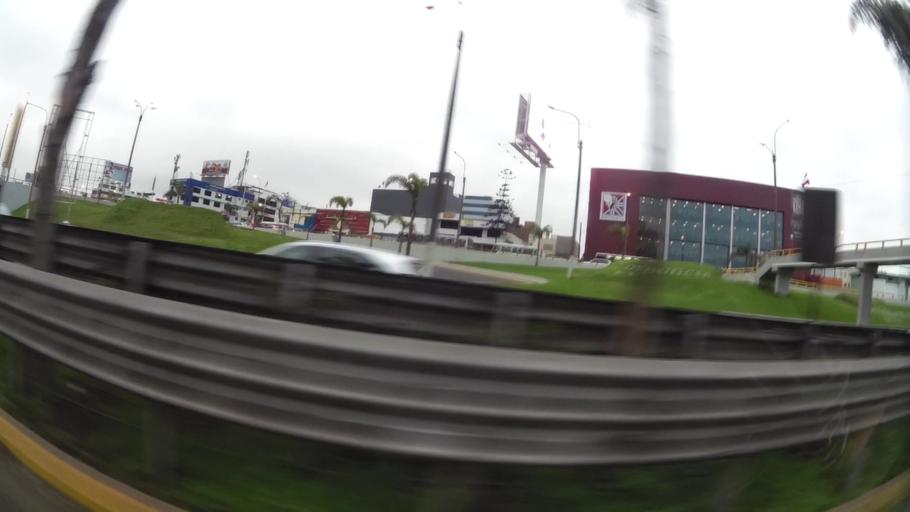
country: PE
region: Lima
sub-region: Lima
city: San Luis
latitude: -12.0869
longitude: -76.9976
